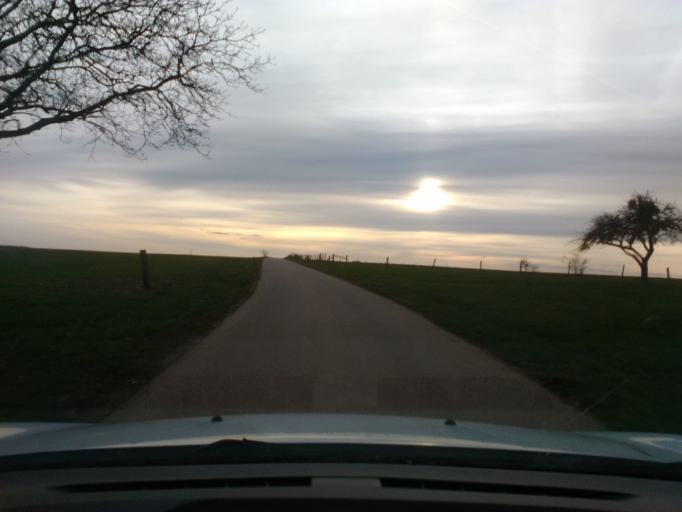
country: FR
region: Lorraine
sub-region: Departement des Vosges
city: Chatel-sur-Moselle
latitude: 48.3666
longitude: 6.5009
